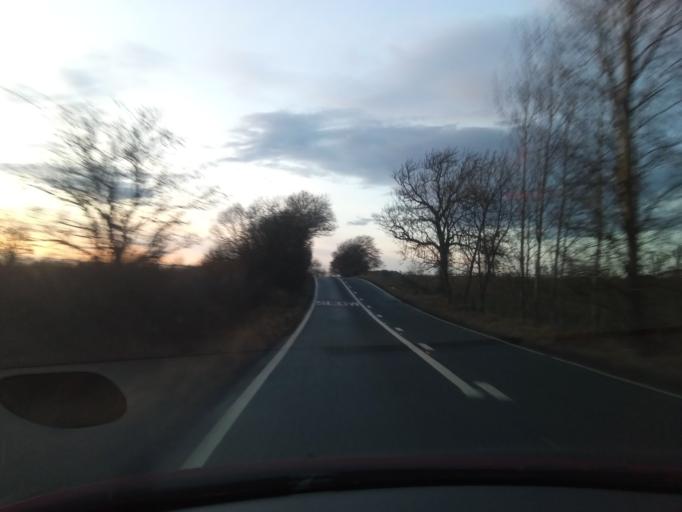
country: GB
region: England
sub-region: Northumberland
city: Otterburn
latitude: 55.2292
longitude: -2.1678
